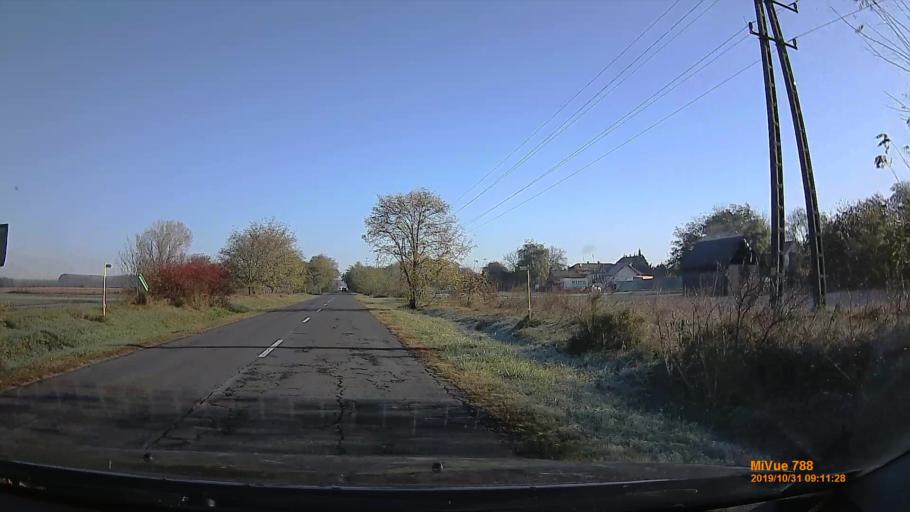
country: HU
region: Pest
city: Peteri
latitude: 47.3670
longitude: 19.3867
